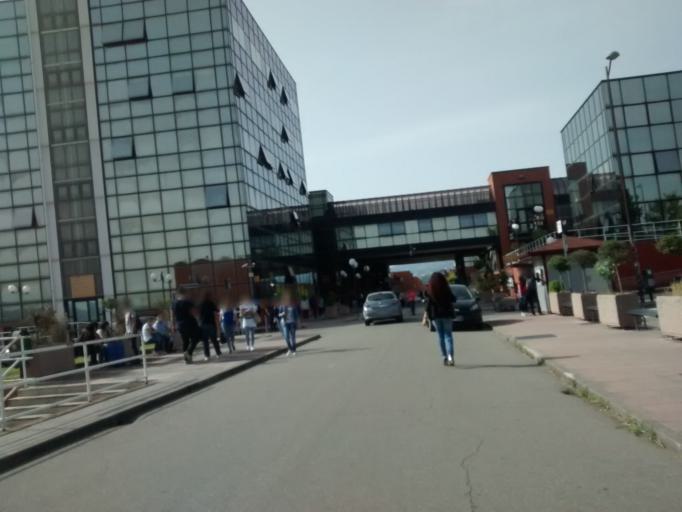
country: IT
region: Calabria
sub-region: Provincia di Cosenza
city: Arcavacata
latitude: 39.3624
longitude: 16.2261
